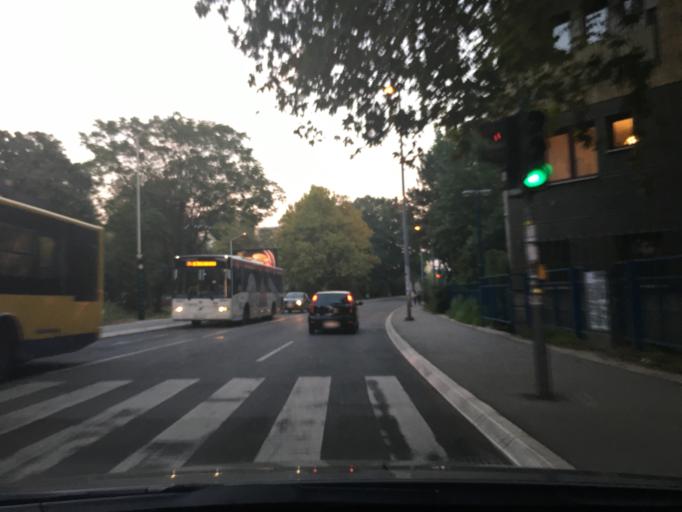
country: RS
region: Central Serbia
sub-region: Belgrade
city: Zemun
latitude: 44.8263
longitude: 20.3994
